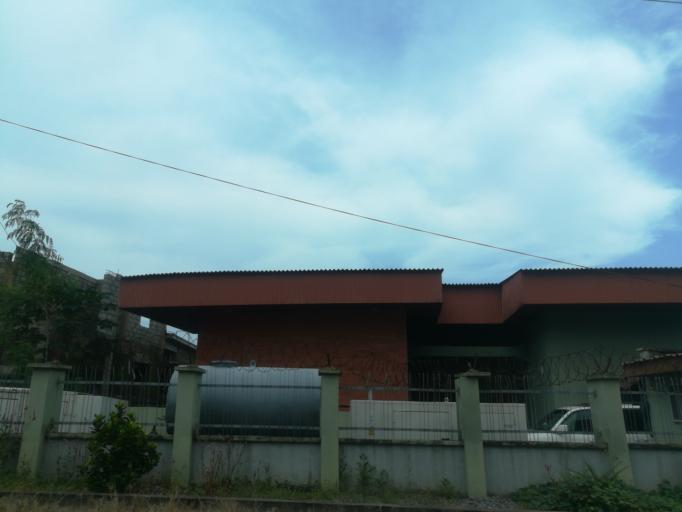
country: NG
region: Oyo
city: Ibadan
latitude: 7.4138
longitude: 3.8994
